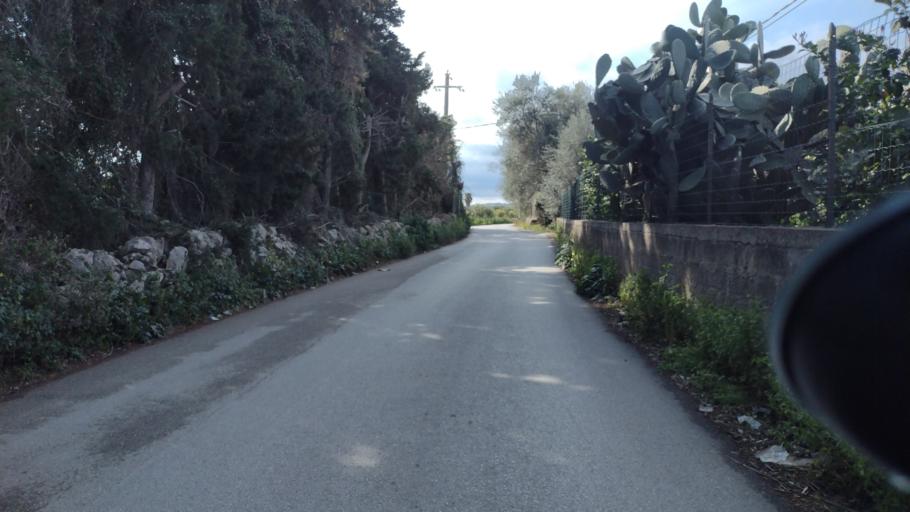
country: IT
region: Sicily
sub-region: Provincia di Siracusa
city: Avola
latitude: 36.8860
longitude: 15.1350
